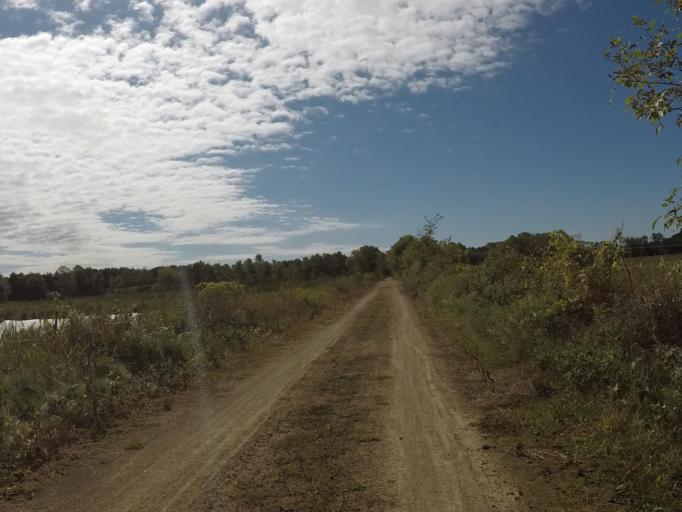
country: US
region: Wisconsin
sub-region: Richland County
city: Richland Center
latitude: 43.2324
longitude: -90.2995
